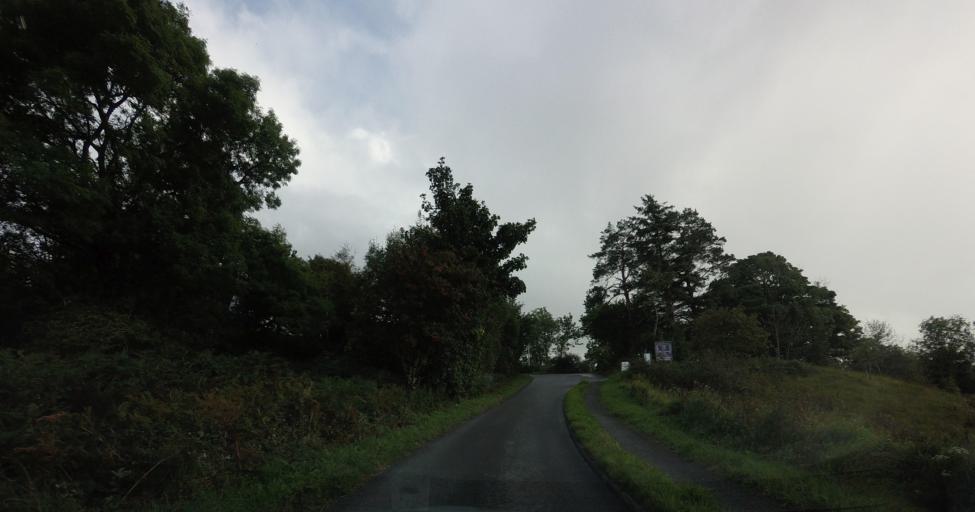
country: GB
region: Scotland
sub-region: Highland
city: Portree
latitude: 57.2150
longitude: -6.0145
